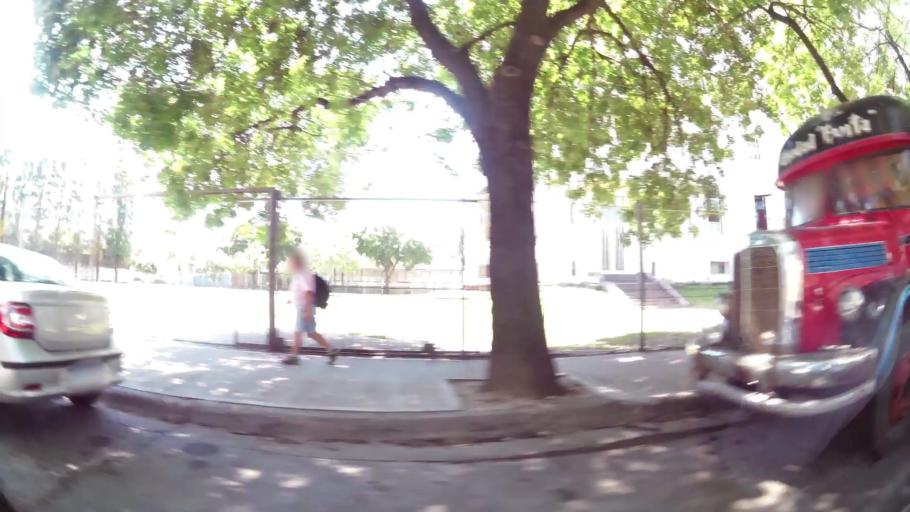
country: AR
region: Buenos Aires
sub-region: Partido de Avellaneda
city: Avellaneda
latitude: -34.6531
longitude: -58.4123
